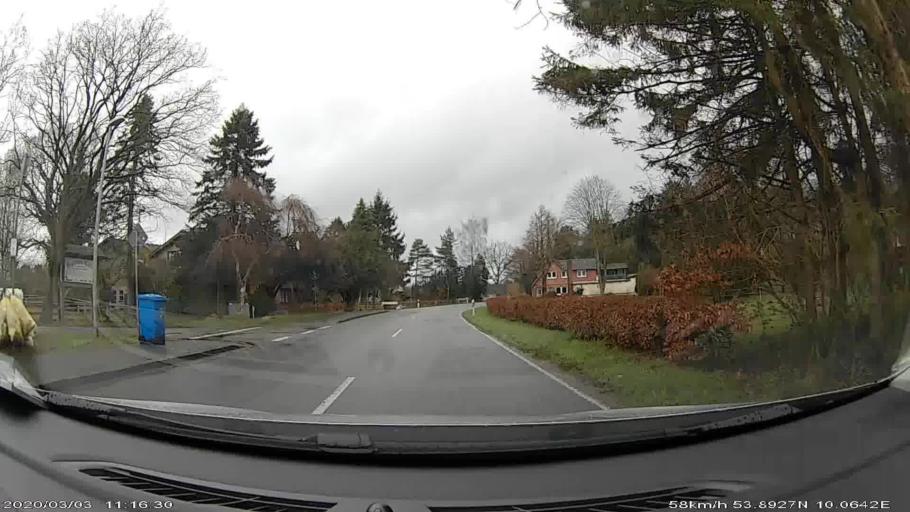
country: DE
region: Schleswig-Holstein
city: Hartenholm
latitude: 53.8950
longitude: 10.0649
